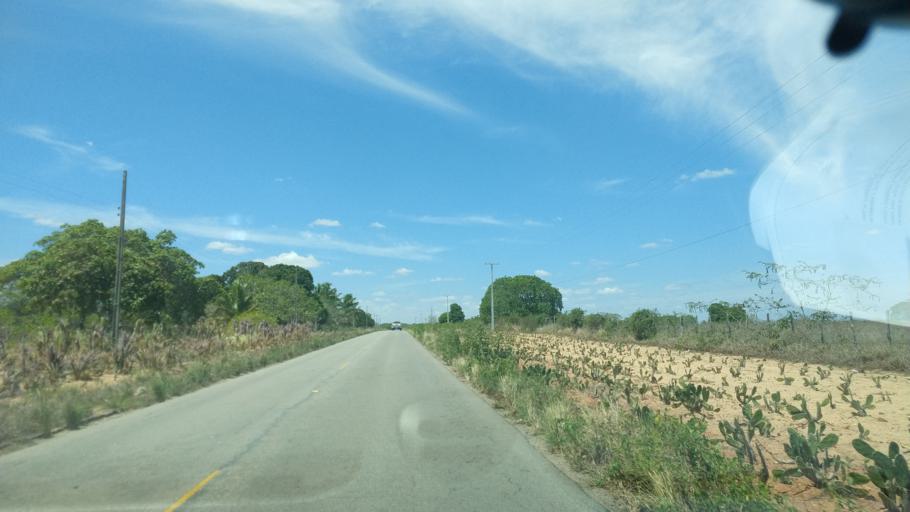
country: BR
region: Rio Grande do Norte
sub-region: Sao Paulo Do Potengi
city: Sao Paulo do Potengi
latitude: -5.9320
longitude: -35.5660
